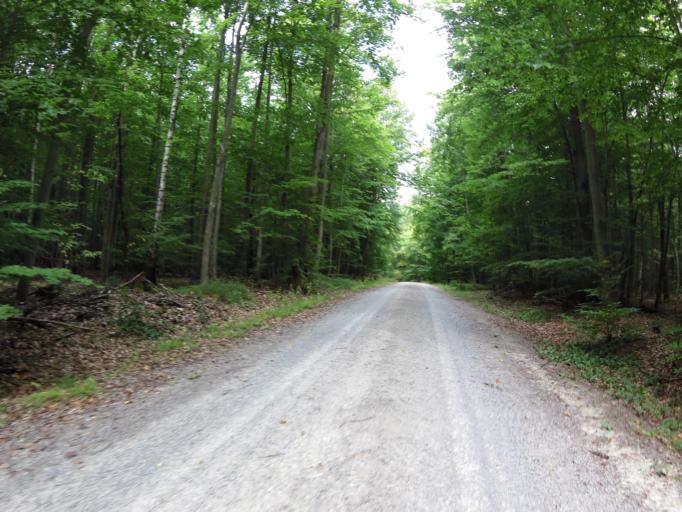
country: DE
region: Bavaria
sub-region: Regierungsbezirk Unterfranken
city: Kleinrinderfeld
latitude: 49.7181
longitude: 9.8152
